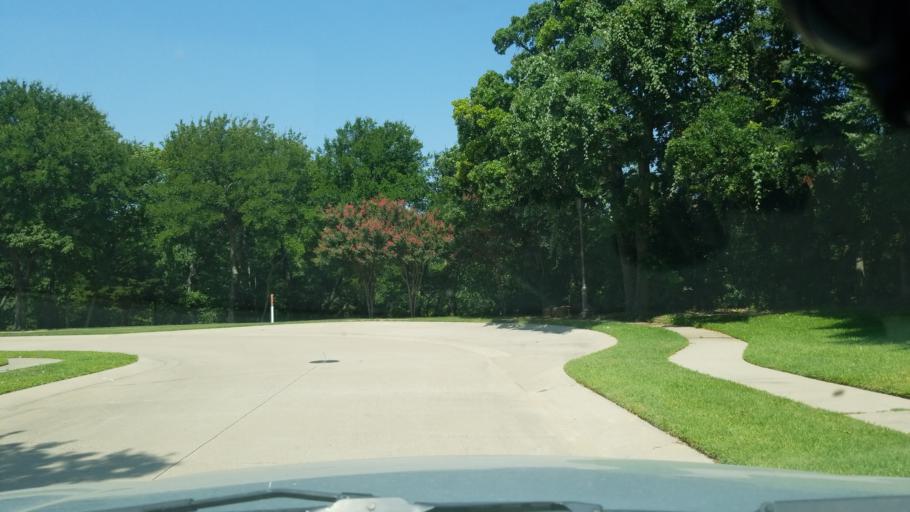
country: US
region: Texas
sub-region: Dallas County
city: Coppell
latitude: 32.9540
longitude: -96.9966
